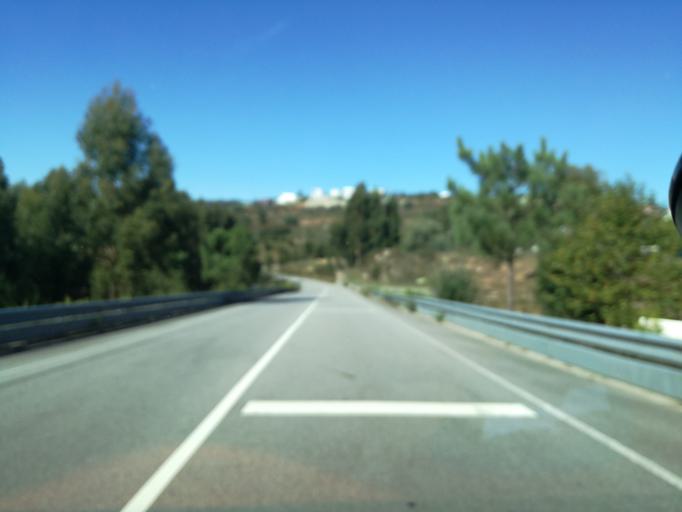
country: PT
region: Porto
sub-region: Pacos de Ferreira
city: Seroa
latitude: 41.2644
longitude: -8.4430
